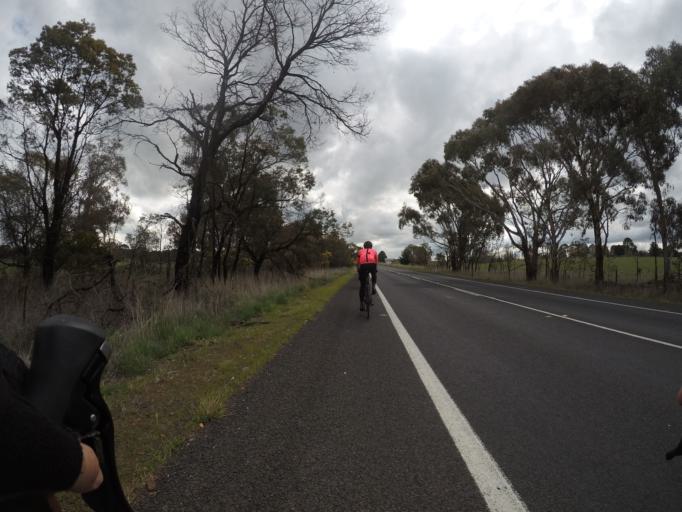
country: AU
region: New South Wales
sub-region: Blayney
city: Blayney
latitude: -33.4333
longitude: 149.3485
